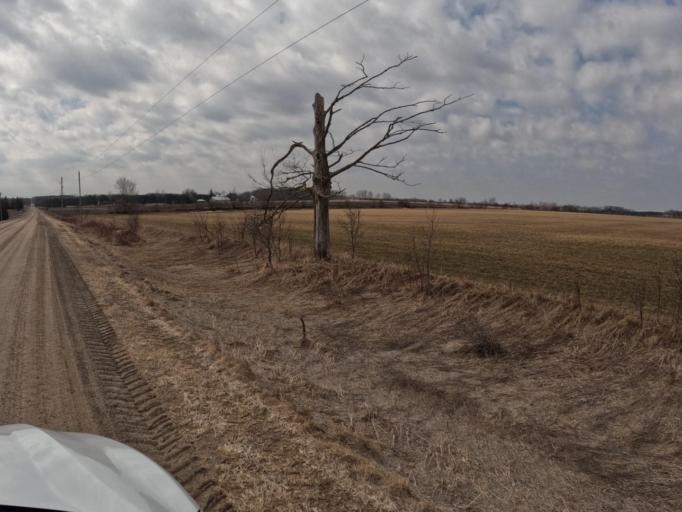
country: CA
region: Ontario
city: Orangeville
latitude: 43.9136
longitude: -80.2381
